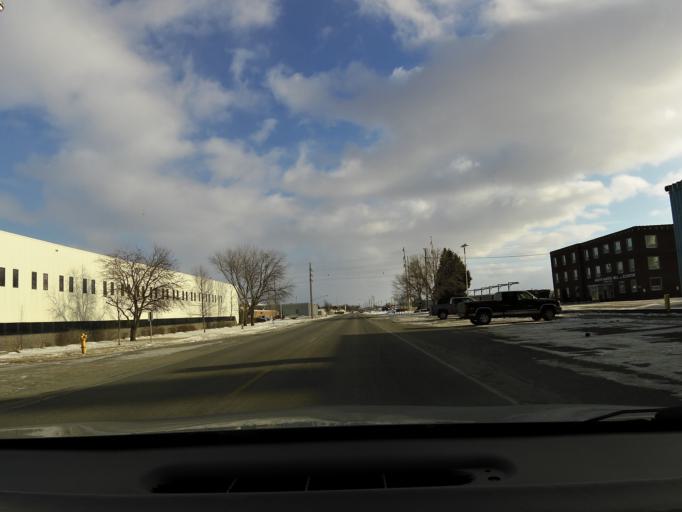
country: US
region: North Dakota
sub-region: Grand Forks County
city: Grand Forks
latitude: 47.9390
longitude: -97.0543
